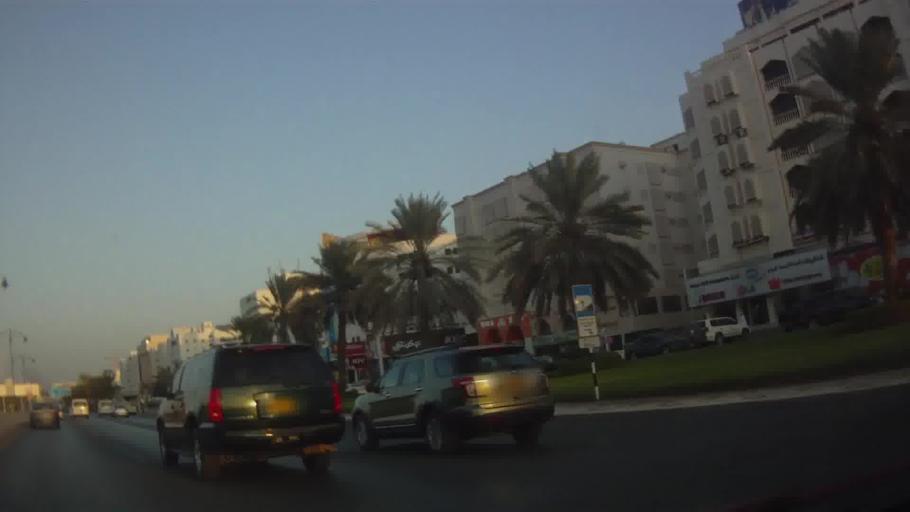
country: OM
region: Muhafazat Masqat
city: Bawshar
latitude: 23.5971
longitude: 58.4263
